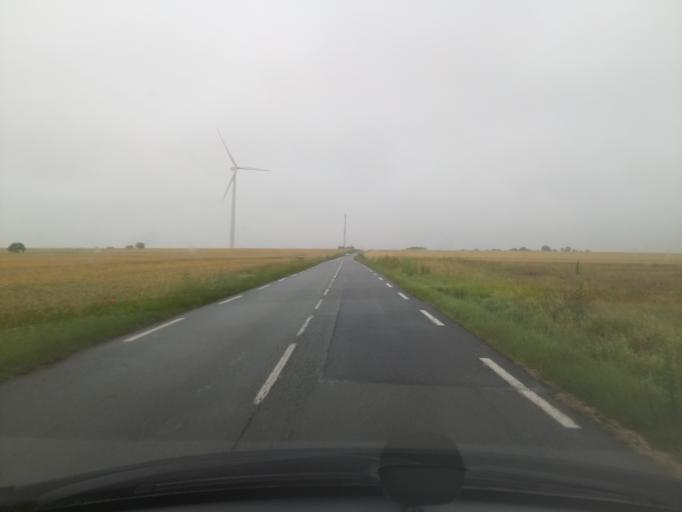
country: FR
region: Poitou-Charentes
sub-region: Departement de la Charente-Maritime
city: Saint-Jean-de-Liversay
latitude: 46.2446
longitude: -0.8813
